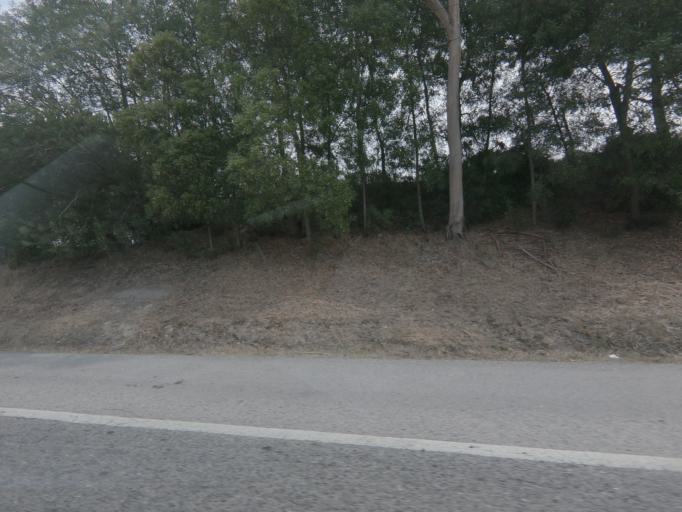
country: PT
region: Leiria
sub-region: Leiria
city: Leiria
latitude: 39.7722
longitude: -8.7668
